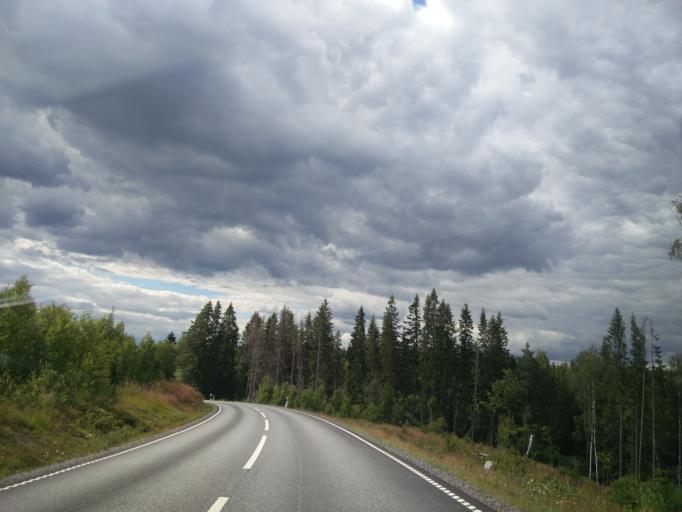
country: SE
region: OErebro
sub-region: Hallefors Kommun
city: Haellefors
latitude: 59.8159
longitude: 14.6599
